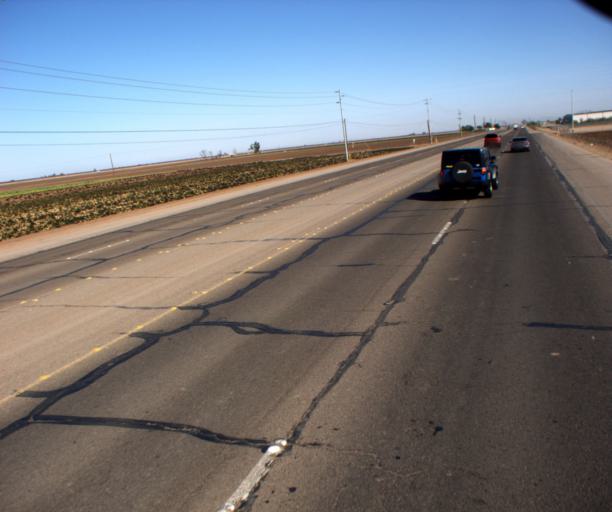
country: US
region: Arizona
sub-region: Yuma County
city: San Luis
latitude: 32.5217
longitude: -114.7866
